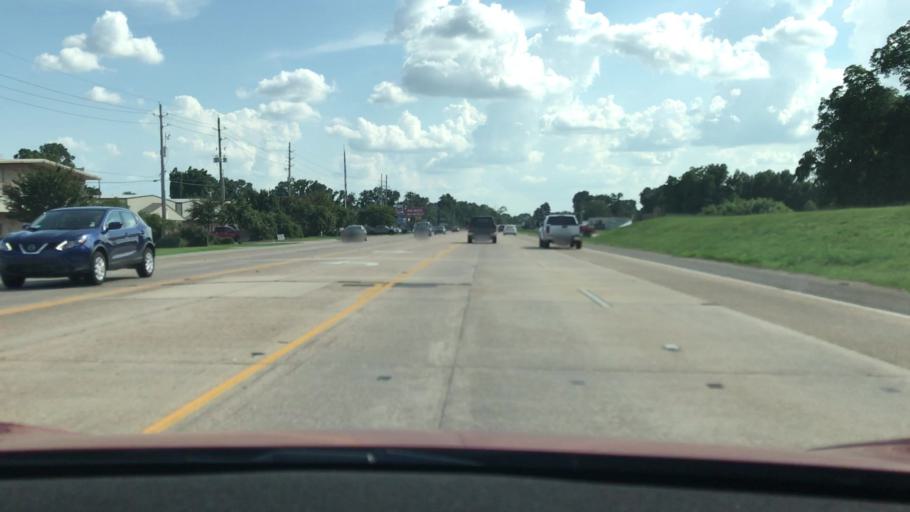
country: US
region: Louisiana
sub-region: Bossier Parish
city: Bossier City
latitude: 32.4523
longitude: -93.6948
